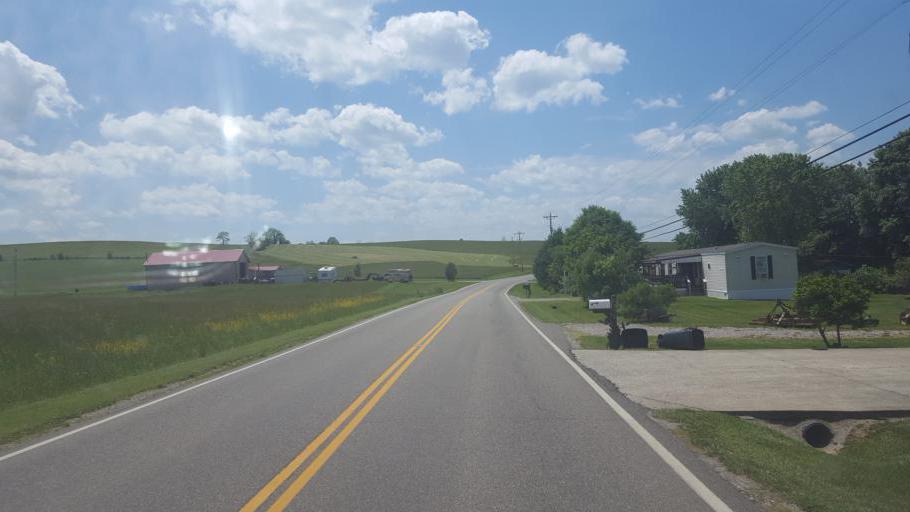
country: US
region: Ohio
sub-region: Jackson County
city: Oak Hill
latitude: 38.8272
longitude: -82.3957
